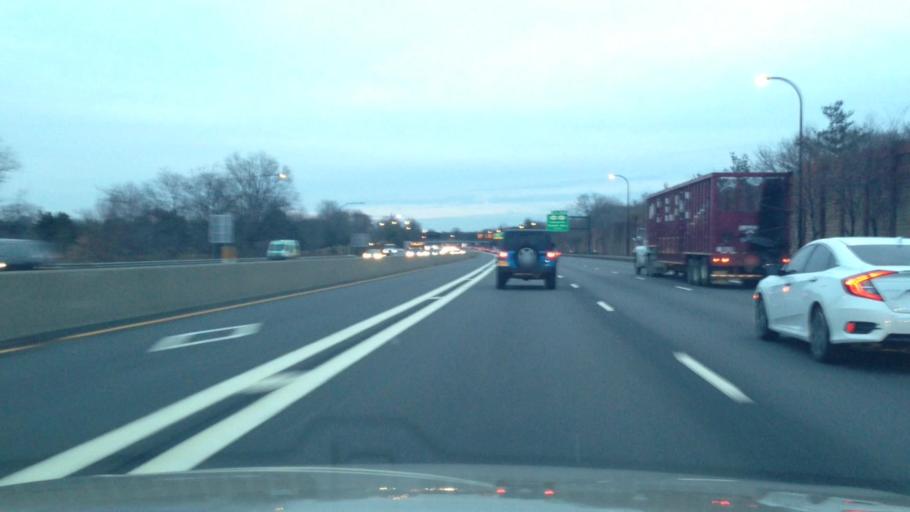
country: US
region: New York
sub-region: Nassau County
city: Jericho
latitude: 40.7832
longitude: -73.5496
